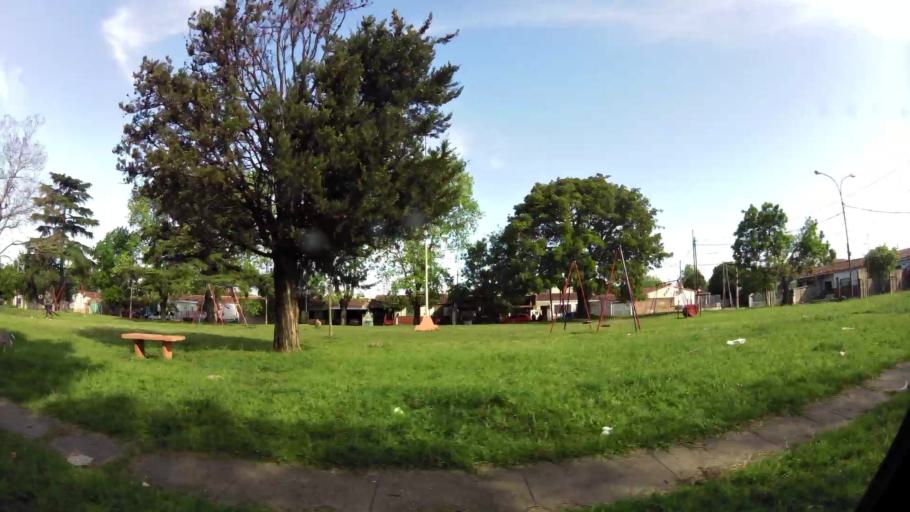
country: AR
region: Buenos Aires
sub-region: Partido de Quilmes
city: Quilmes
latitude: -34.7910
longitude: -58.2316
